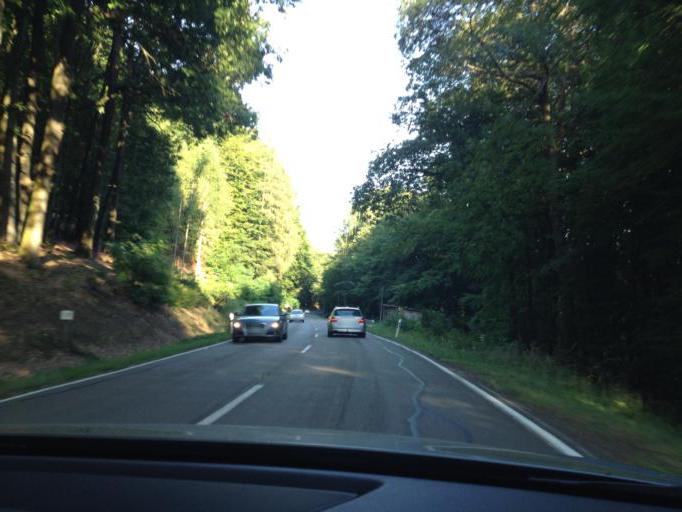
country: DE
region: Saarland
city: Tholey
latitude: 49.5172
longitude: 7.0518
